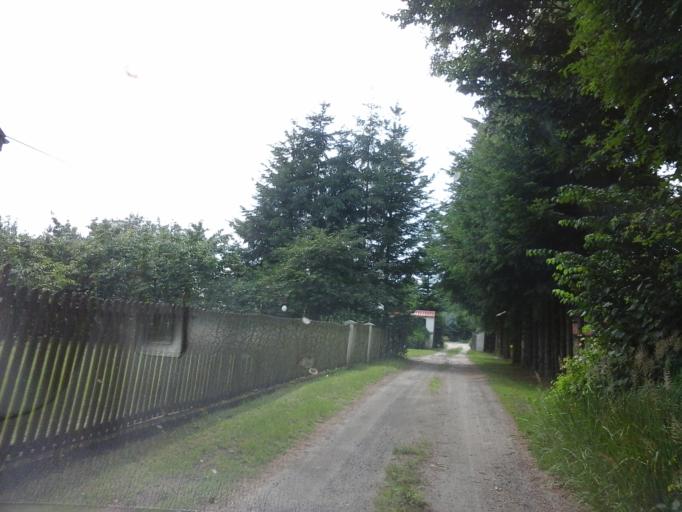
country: PL
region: Lubusz
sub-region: Powiat strzelecko-drezdenecki
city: Dobiegniew
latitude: 53.0926
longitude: 15.7807
